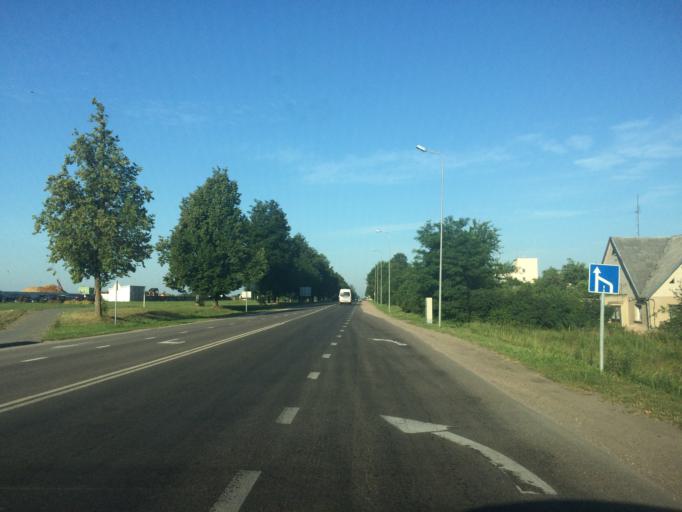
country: LT
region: Vilnius County
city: Ukmerge
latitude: 55.2393
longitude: 24.7357
